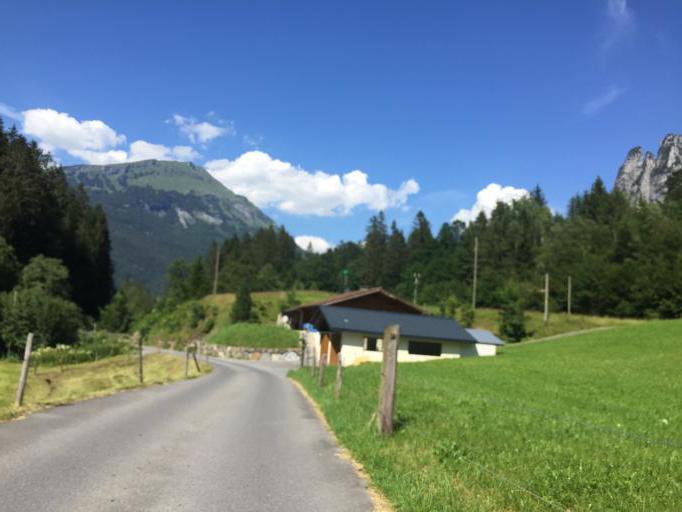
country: CH
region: Bern
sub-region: Interlaken-Oberhasli District
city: Meiringen
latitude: 46.6929
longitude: 8.2253
